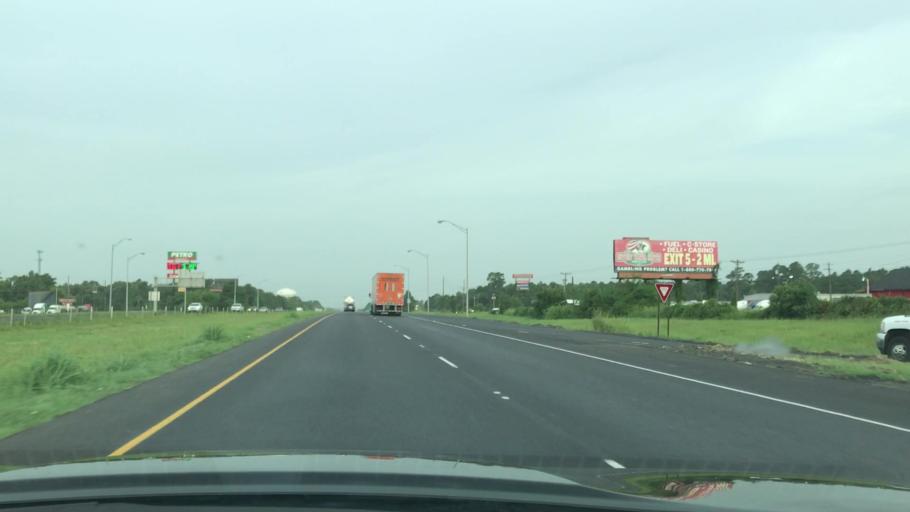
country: US
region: Louisiana
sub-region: Caddo Parish
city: Greenwood
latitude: 32.4474
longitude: -93.9010
